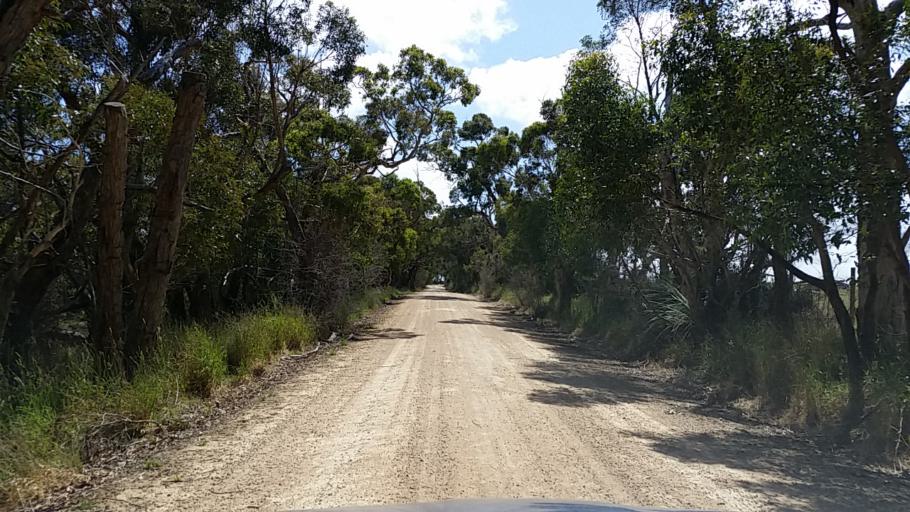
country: AU
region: South Australia
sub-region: Alexandrina
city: Port Elliot
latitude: -35.4509
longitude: 138.6555
